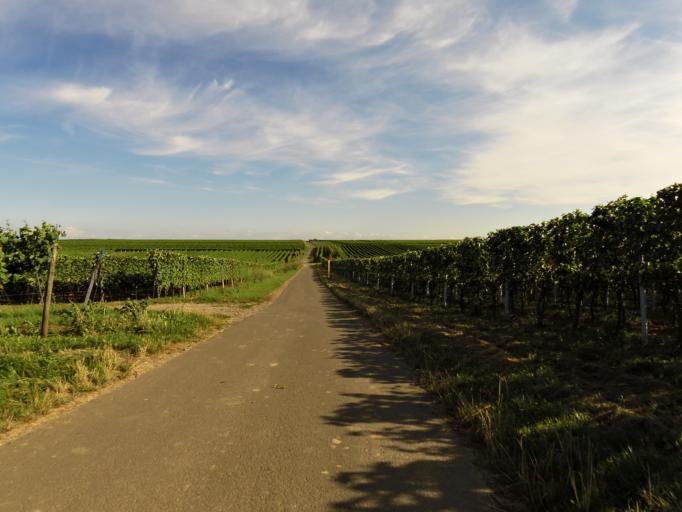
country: DE
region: Rheinland-Pfalz
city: Bissersheim
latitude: 49.5289
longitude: 8.1982
